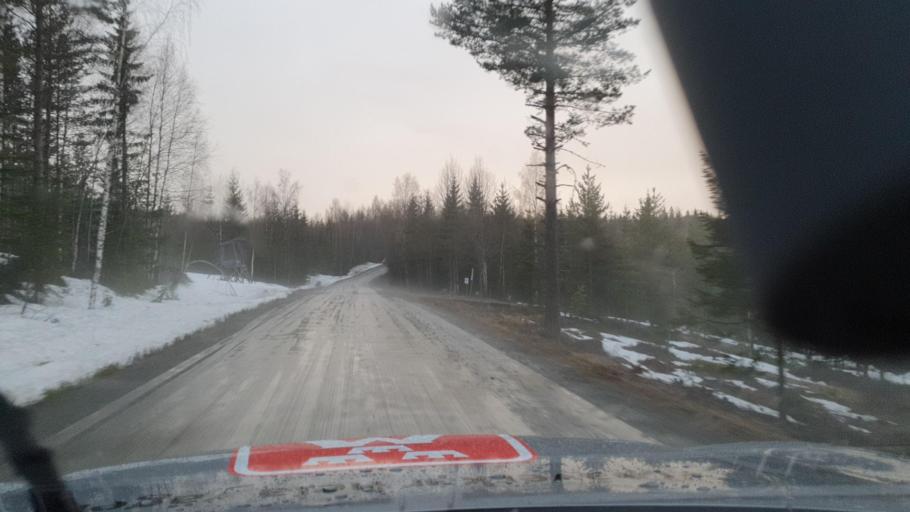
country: SE
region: Vaesternorrland
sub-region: OErnskoeldsviks Kommun
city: Bjasta
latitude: 63.2102
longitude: 18.2952
